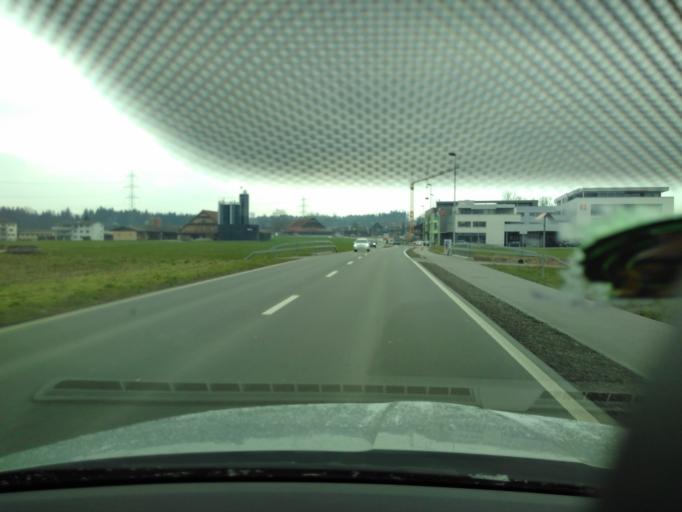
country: CH
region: Lucerne
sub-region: Hochdorf District
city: Inwil
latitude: 47.1182
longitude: 8.3418
